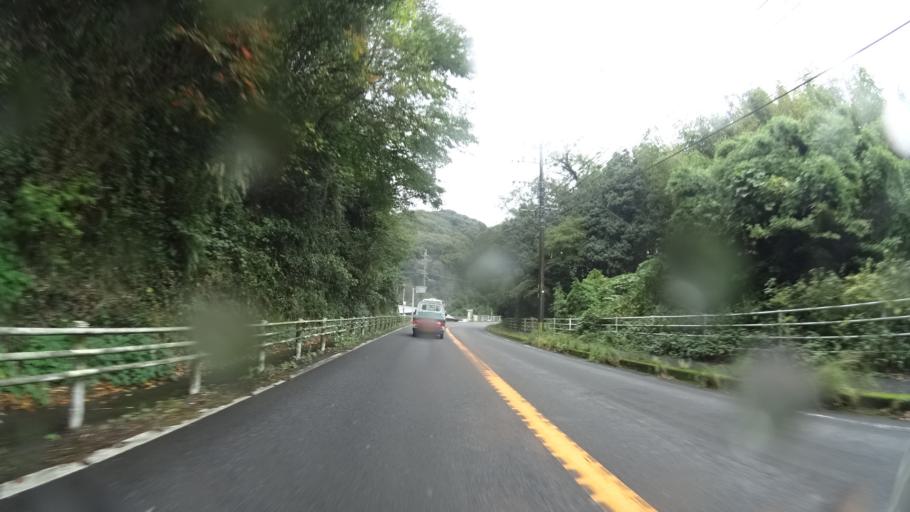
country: JP
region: Kagoshima
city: Kajiki
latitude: 31.7645
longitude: 130.6714
